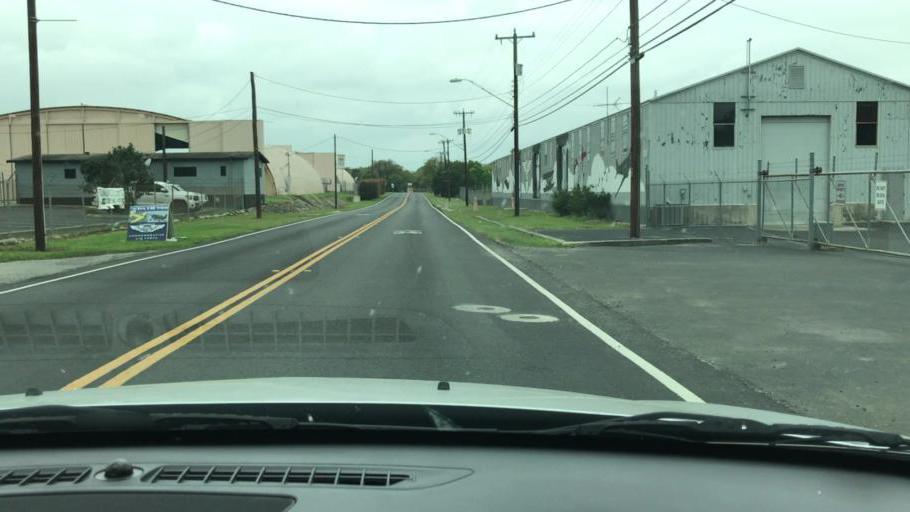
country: US
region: Texas
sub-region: Bexar County
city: San Antonio
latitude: 29.3405
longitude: -98.4689
